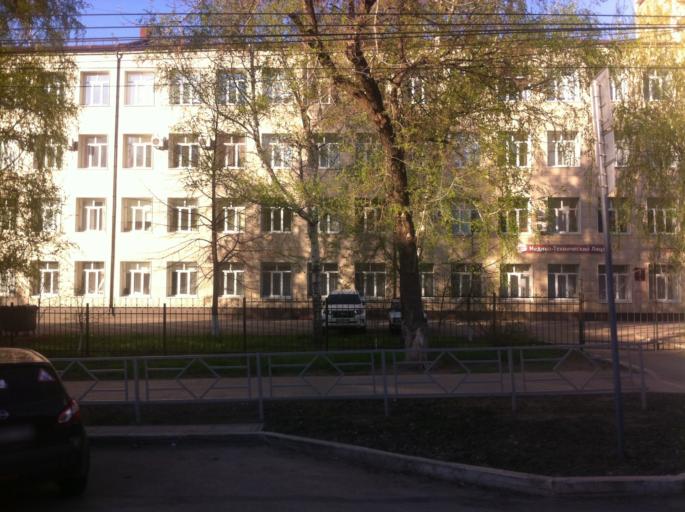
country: RU
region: Samara
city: Samara
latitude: 53.2040
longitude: 50.1254
